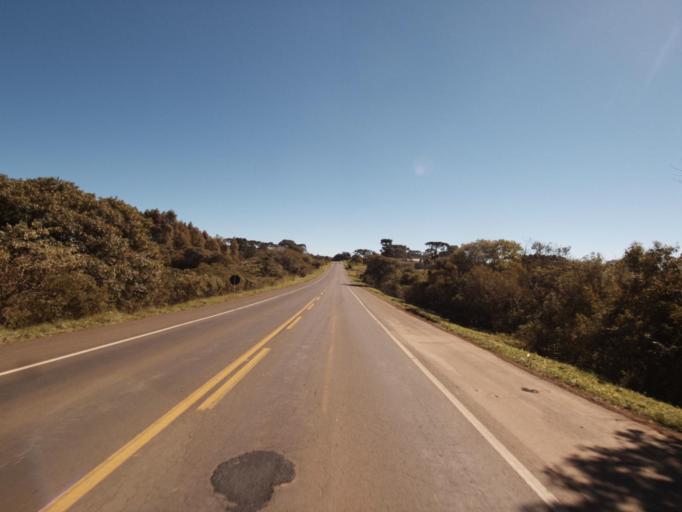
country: BR
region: Santa Catarina
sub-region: Xanxere
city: Xanxere
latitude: -26.8582
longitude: -52.2430
